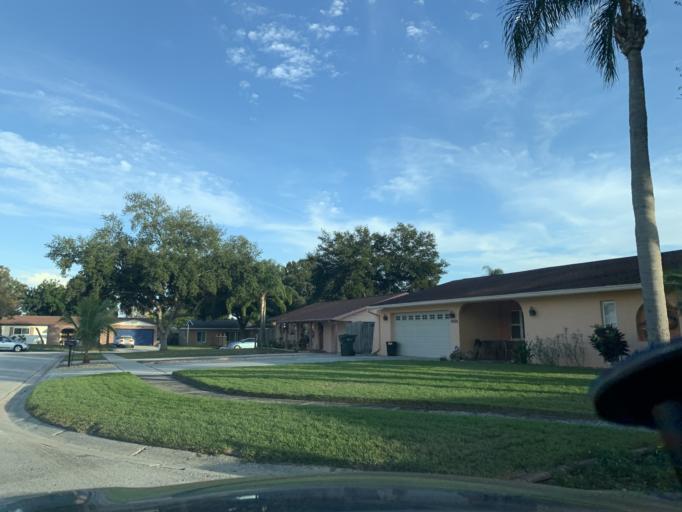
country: US
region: Florida
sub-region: Pinellas County
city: Ridgecrest
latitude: 27.8888
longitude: -82.7965
